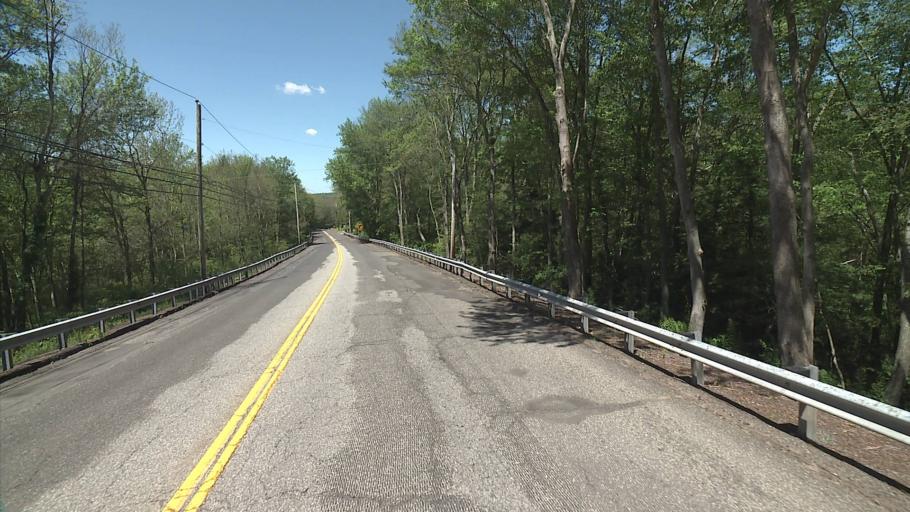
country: US
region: Connecticut
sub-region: Middlesex County
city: Moodus
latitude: 41.5495
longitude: -72.4389
